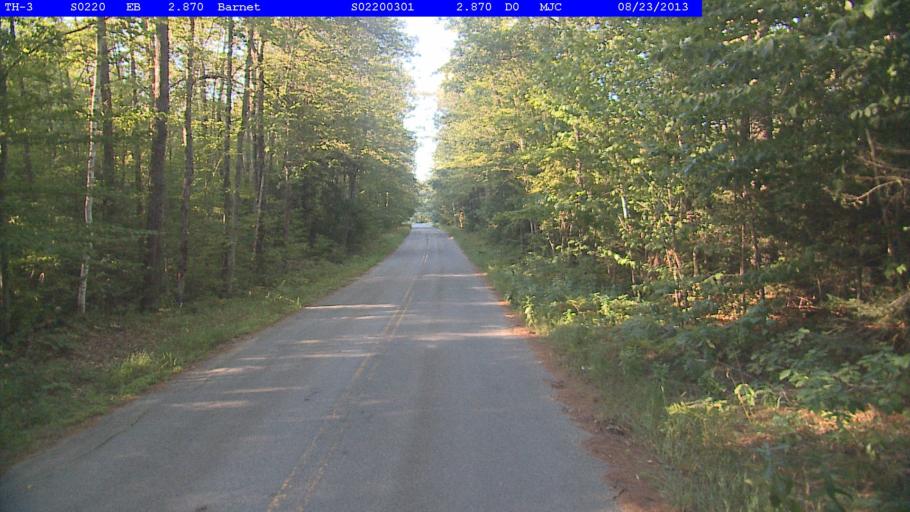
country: US
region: Vermont
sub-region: Caledonia County
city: Saint Johnsbury
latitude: 44.3354
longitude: -71.9977
